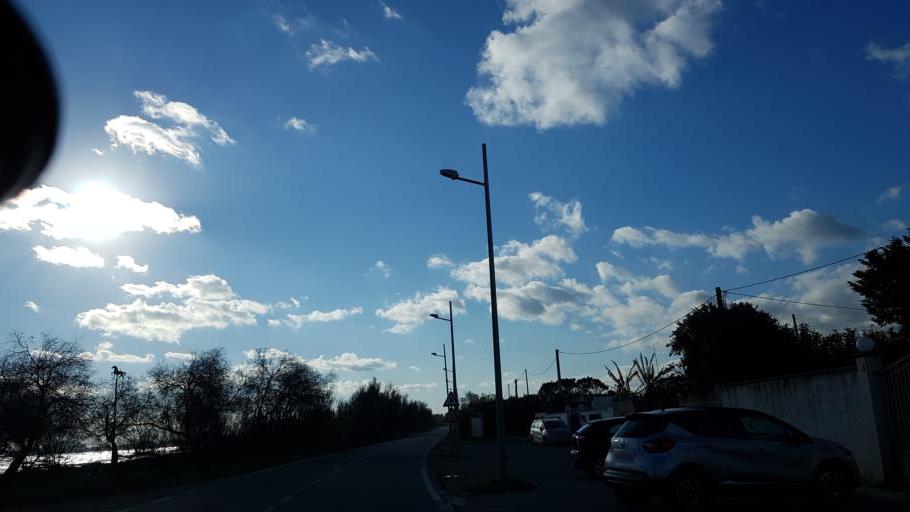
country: IT
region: Apulia
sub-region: Provincia di Brindisi
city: Materdomini
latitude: 40.6746
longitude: 17.9450
